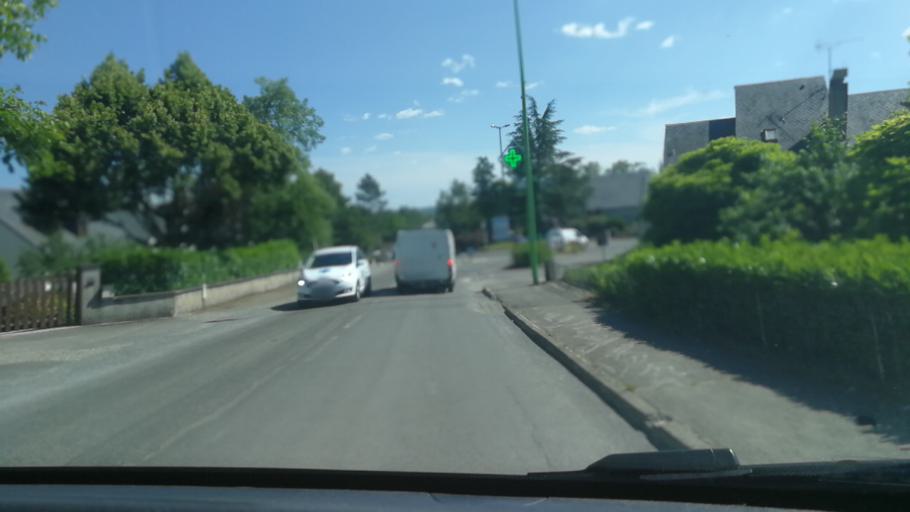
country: FR
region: Midi-Pyrenees
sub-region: Departement de l'Aveyron
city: Sebazac-Concoures
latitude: 44.4019
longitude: 2.5991
